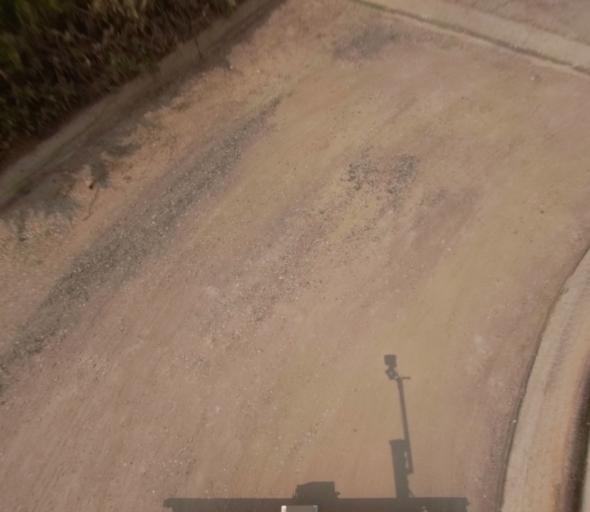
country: US
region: California
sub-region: Madera County
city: Coarsegold
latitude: 37.2646
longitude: -119.6923
